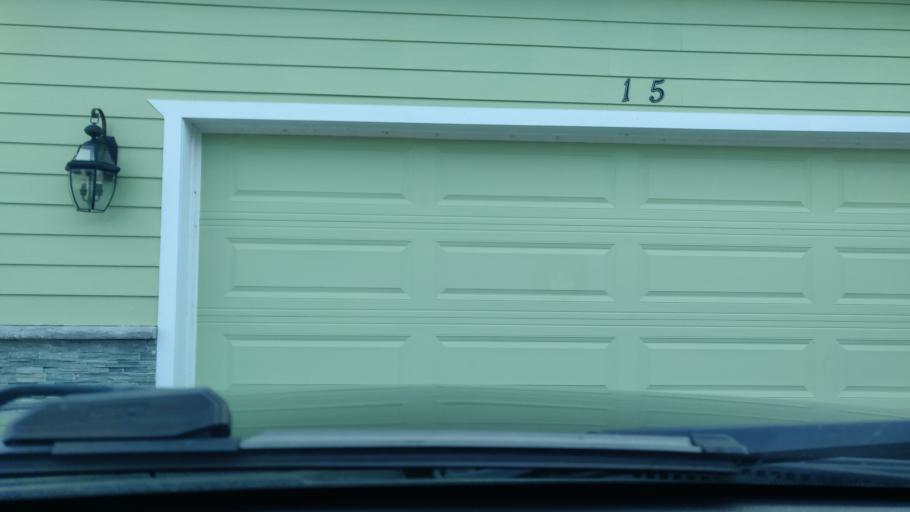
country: US
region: Florida
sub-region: Flagler County
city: Flagler Beach
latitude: 29.5072
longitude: -81.1569
